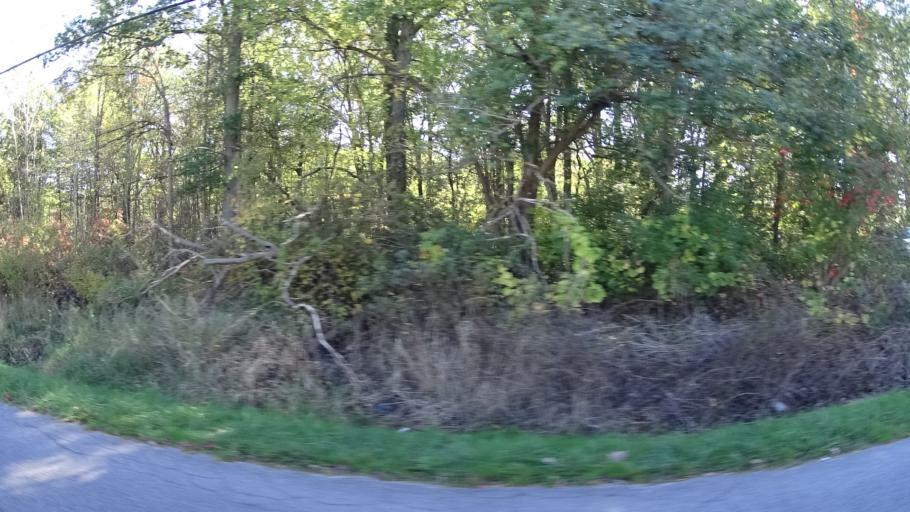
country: US
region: Ohio
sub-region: Lorain County
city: Sheffield
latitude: 41.4172
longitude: -82.1409
